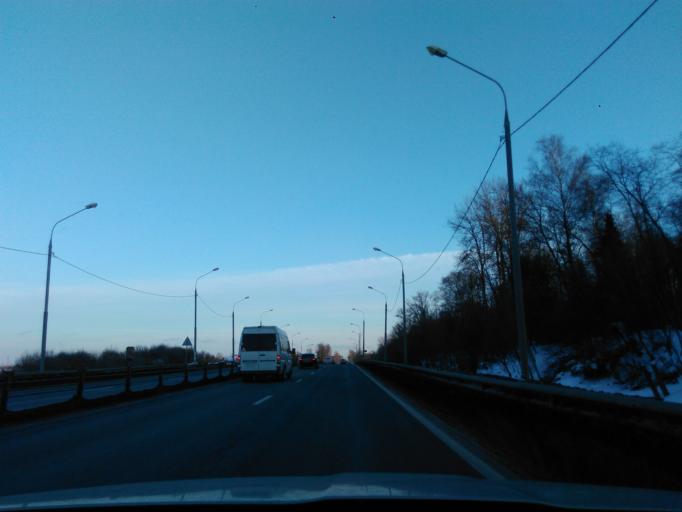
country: RU
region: Moskovskaya
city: Klin
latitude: 56.2923
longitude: 36.8081
